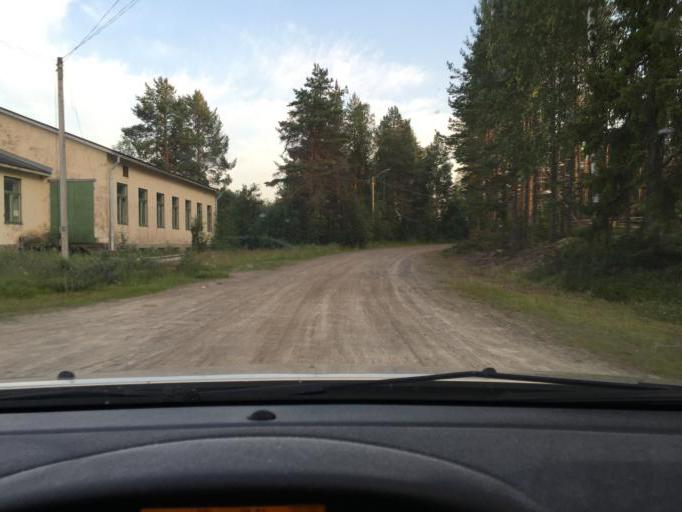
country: SE
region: Norrbotten
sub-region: Kalix Kommun
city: Toere
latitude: 66.0736
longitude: 22.7284
